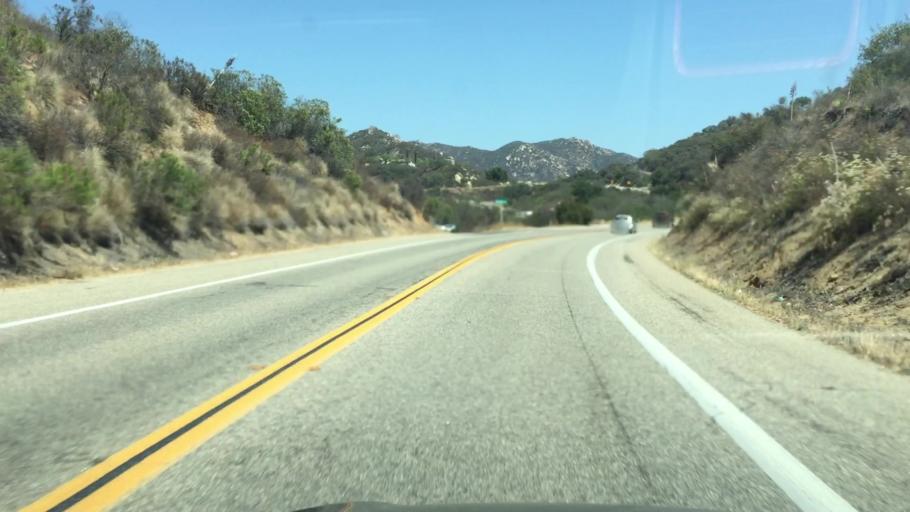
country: US
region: California
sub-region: San Diego County
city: Jamul
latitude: 32.7345
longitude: -116.8263
